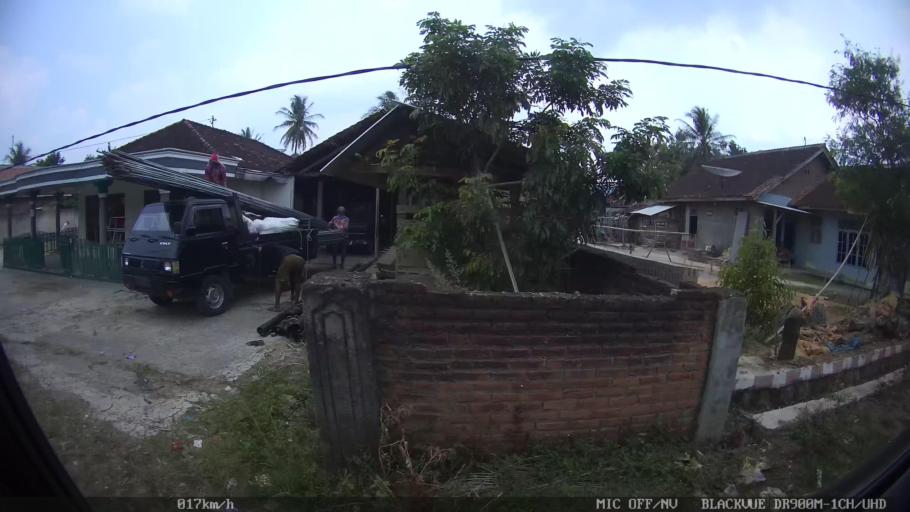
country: ID
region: Lampung
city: Gadingrejo
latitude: -5.3929
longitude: 105.0373
